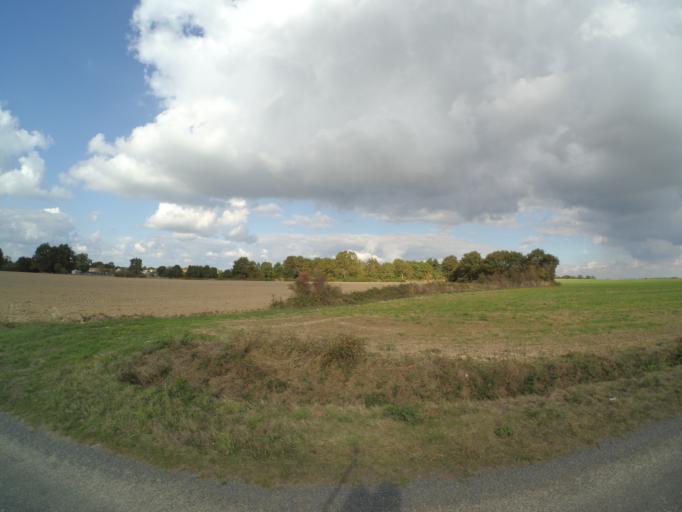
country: FR
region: Pays de la Loire
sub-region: Departement de la Loire-Atlantique
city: Remouille
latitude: 47.0723
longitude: -1.3633
